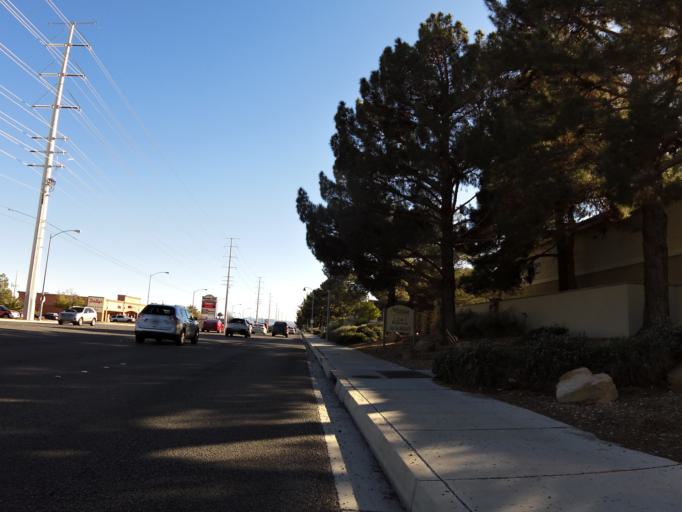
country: US
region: Nevada
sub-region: Clark County
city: Spring Valley
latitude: 36.1369
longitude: -115.2789
